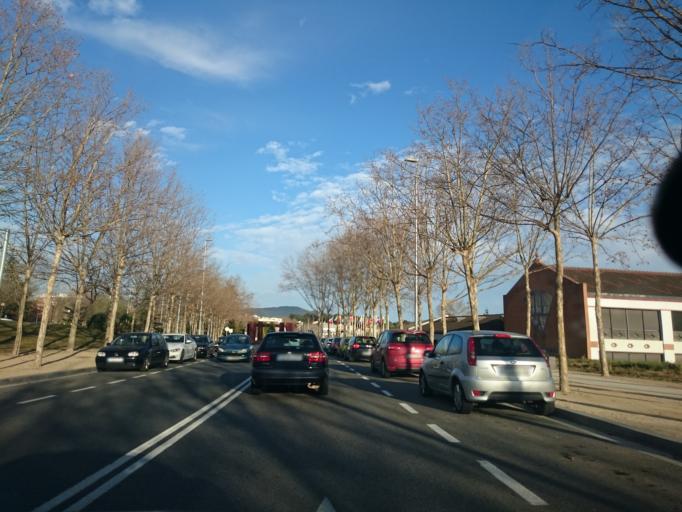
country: ES
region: Catalonia
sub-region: Provincia de Barcelona
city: Cerdanyola del Valles
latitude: 41.4852
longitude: 2.1264
